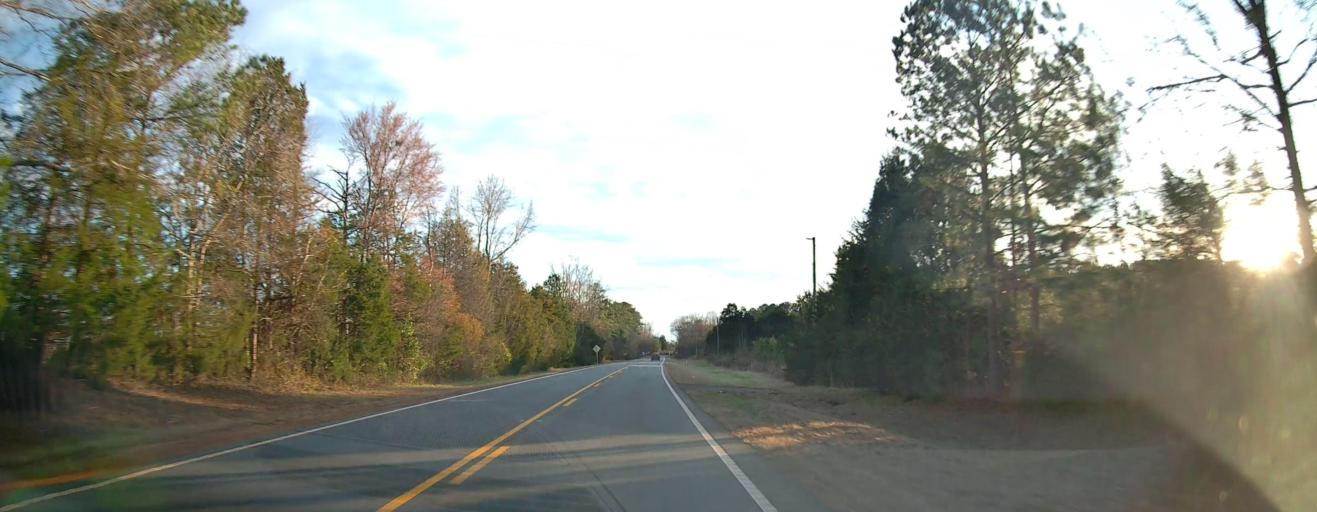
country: US
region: Georgia
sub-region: Talbot County
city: Sardis
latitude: 32.6977
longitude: -84.7010
